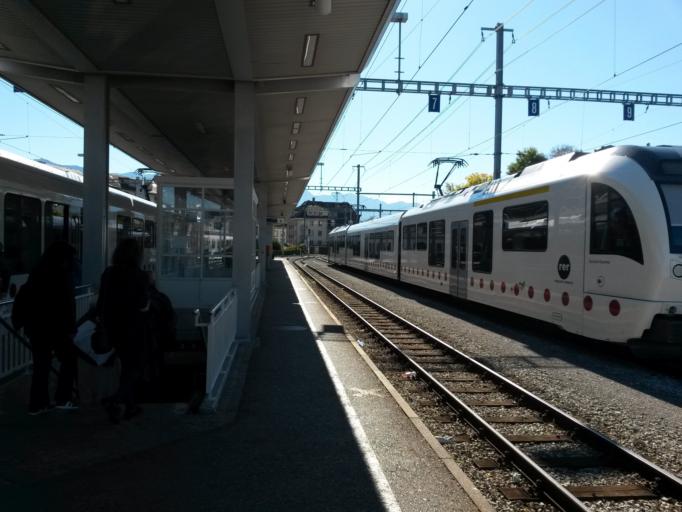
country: CH
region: Fribourg
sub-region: Gruyere District
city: Bulle
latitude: 46.6181
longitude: 7.0544
